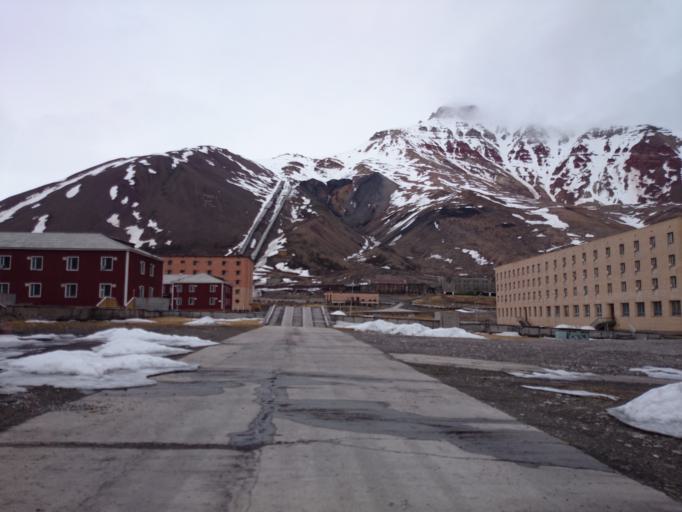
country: SJ
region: Svalbard
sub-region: Spitsbergen
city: Longyearbyen
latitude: 78.6548
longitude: 16.3249
